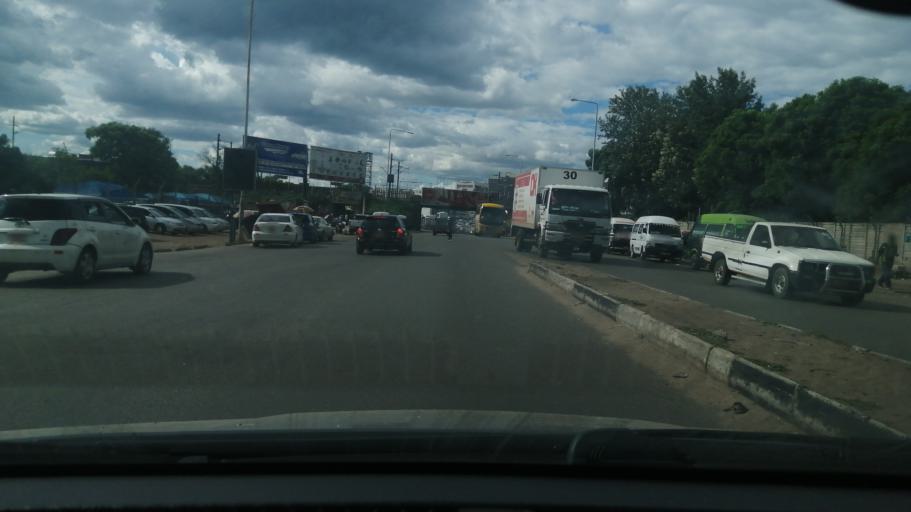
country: ZW
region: Harare
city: Harare
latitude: -17.8380
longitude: 31.0476
